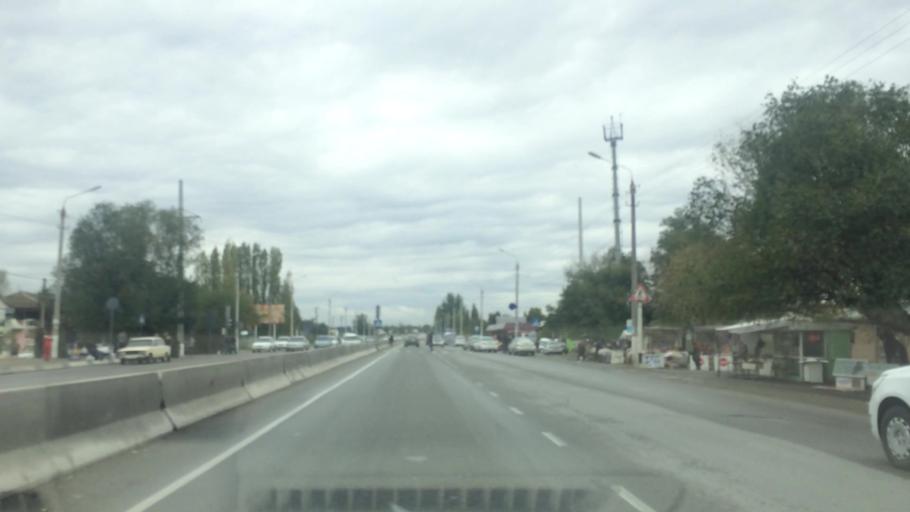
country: UZ
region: Jizzax
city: Jizzax
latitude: 39.9834
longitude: 67.5729
